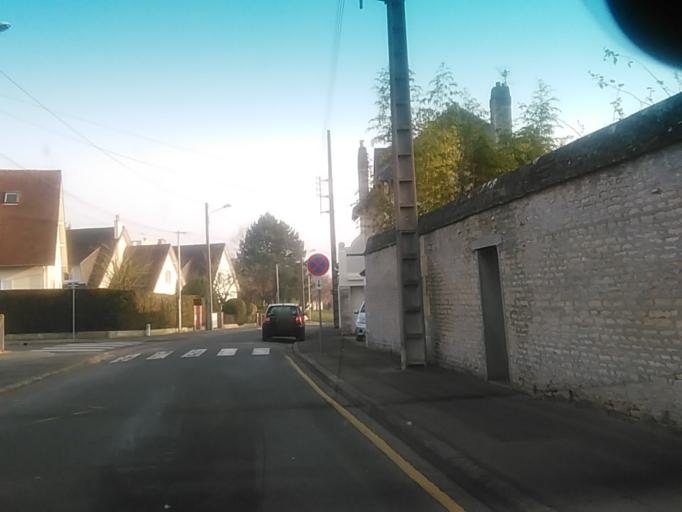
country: FR
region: Lower Normandy
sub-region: Departement du Calvados
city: Saint-Germain-la-Blanche-Herbe
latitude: 49.1774
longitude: -0.3866
